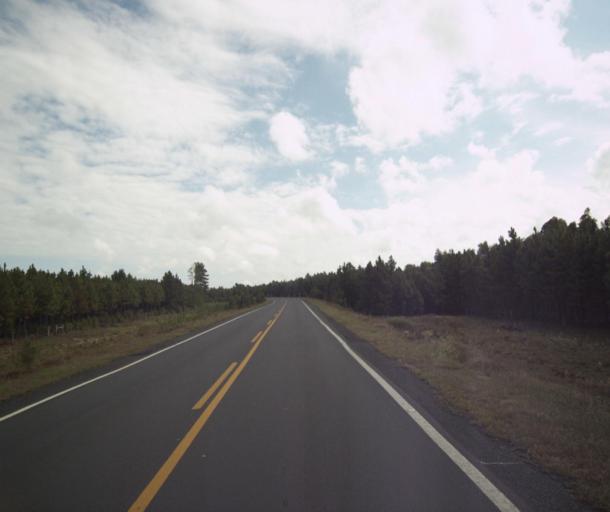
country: BR
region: Rio Grande do Sul
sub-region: Sao Lourenco Do Sul
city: Sao Lourenco do Sul
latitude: -31.4629
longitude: -51.2303
